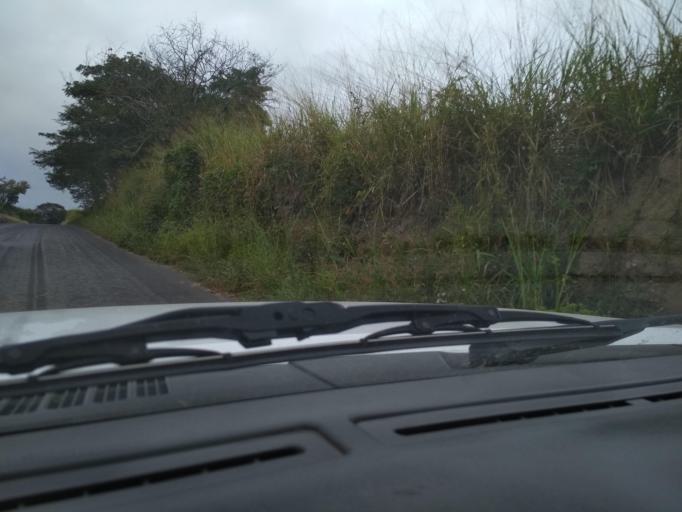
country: MX
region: Veracruz
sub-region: Emiliano Zapata
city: Dos Rios
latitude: 19.5299
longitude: -96.7982
